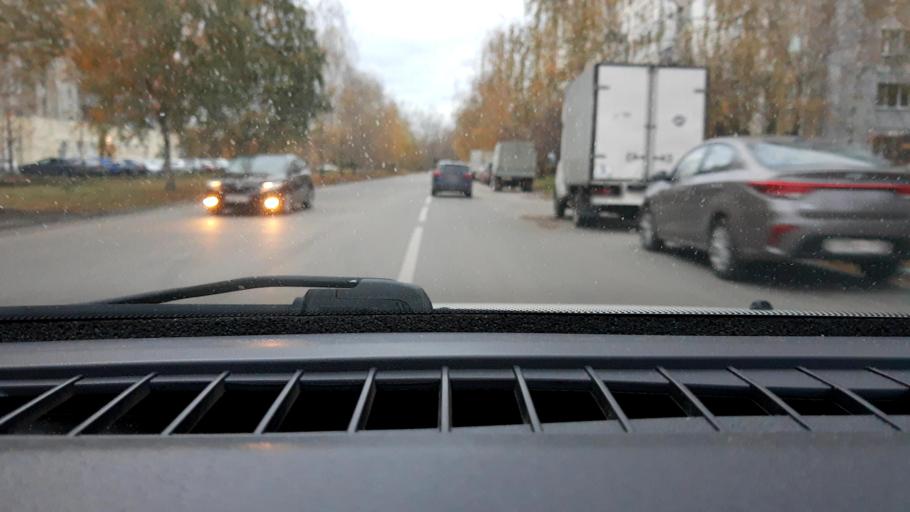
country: RU
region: Nizjnij Novgorod
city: Nizhniy Novgorod
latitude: 56.3273
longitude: 43.8654
